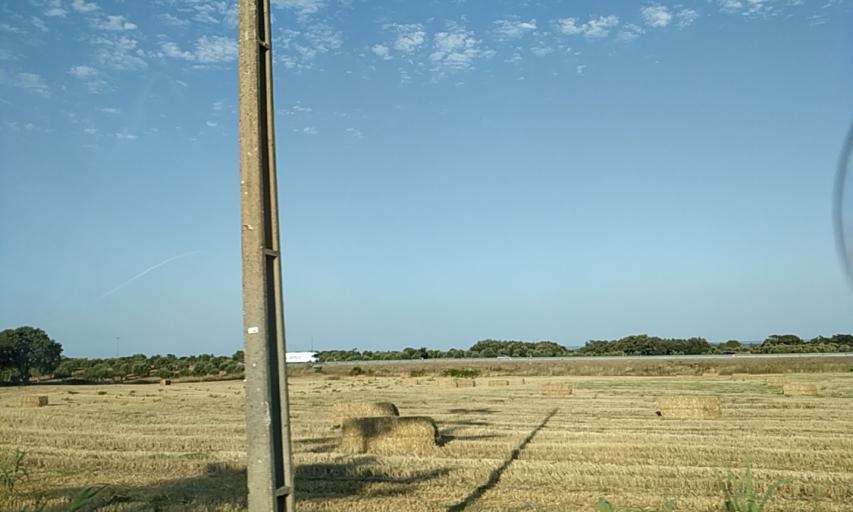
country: PT
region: Santarem
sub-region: Alcanena
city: Alcanena
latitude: 39.4135
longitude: -8.6375
